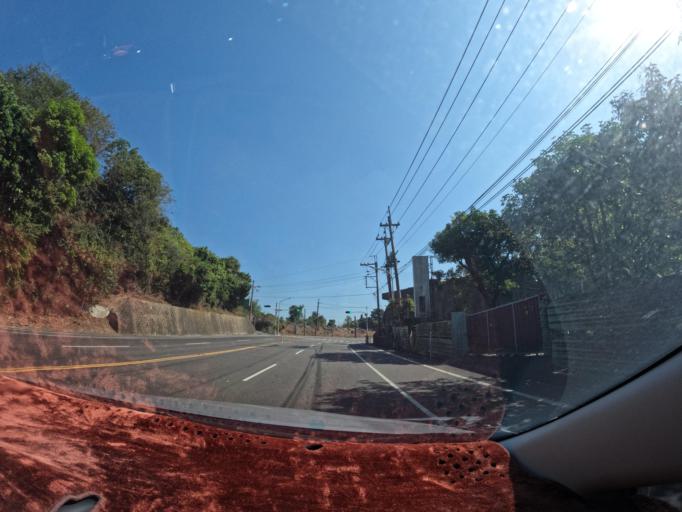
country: TW
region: Taiwan
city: Yujing
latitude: 23.0588
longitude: 120.3960
